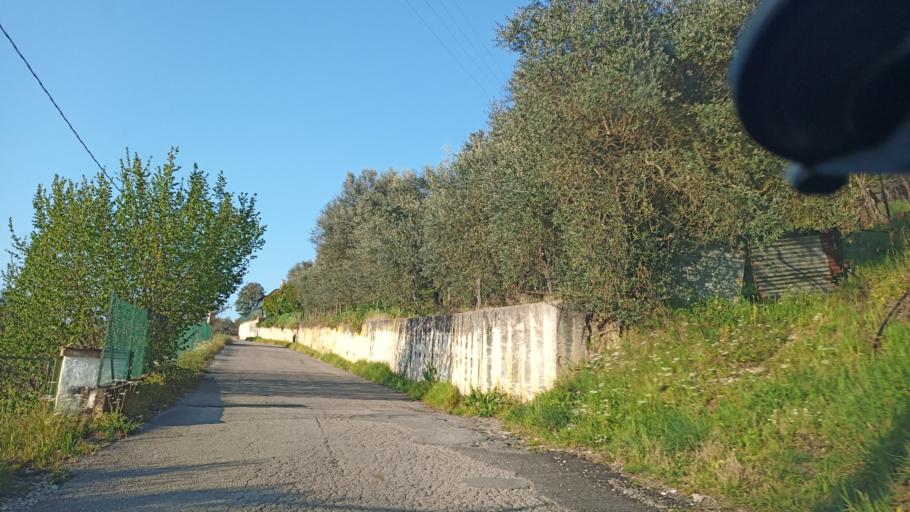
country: IT
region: Latium
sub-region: Provincia di Rieti
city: Poggio Mirteto
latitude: 42.2640
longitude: 12.6798
